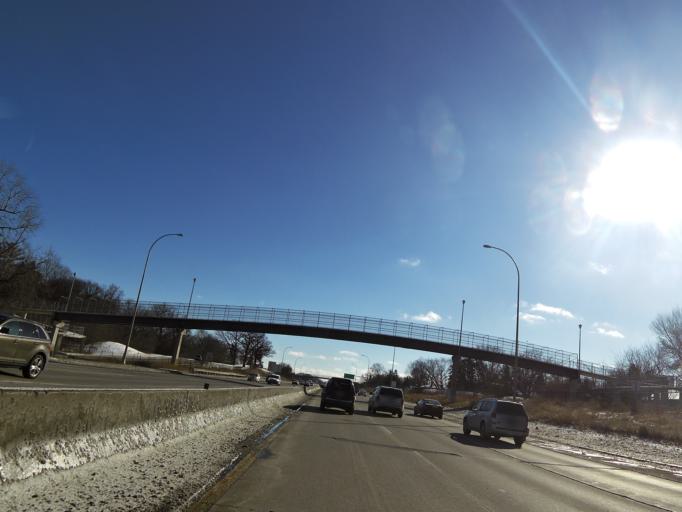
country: US
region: Minnesota
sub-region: Hennepin County
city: Edina
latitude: 44.9047
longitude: -93.3500
